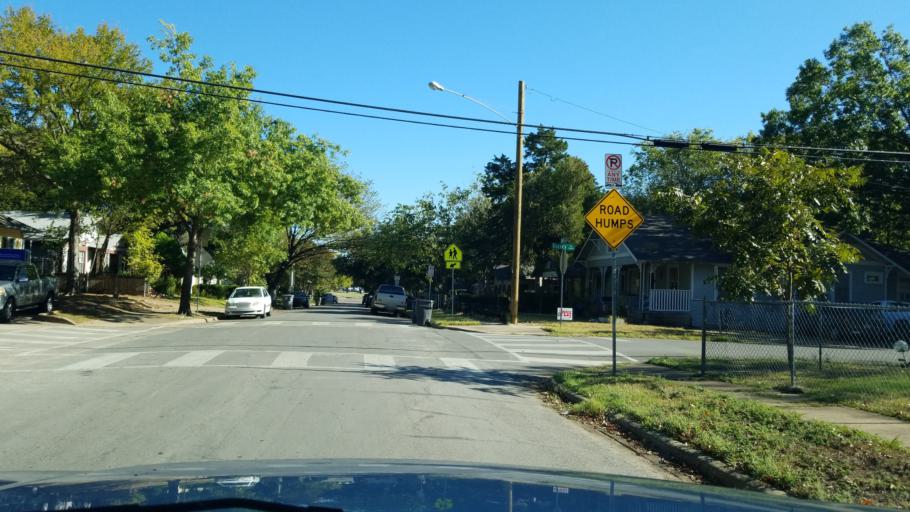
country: US
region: Texas
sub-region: Dallas County
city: Highland Park
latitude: 32.7961
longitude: -96.7485
